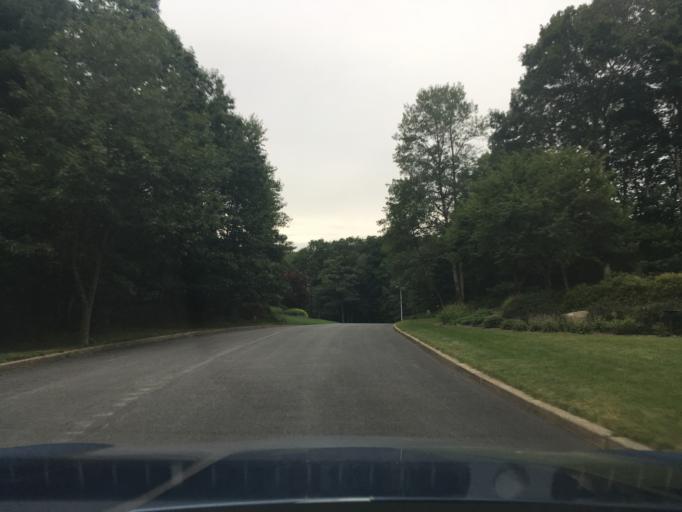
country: US
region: Rhode Island
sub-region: Kent County
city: East Greenwich
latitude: 41.6319
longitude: -71.5065
